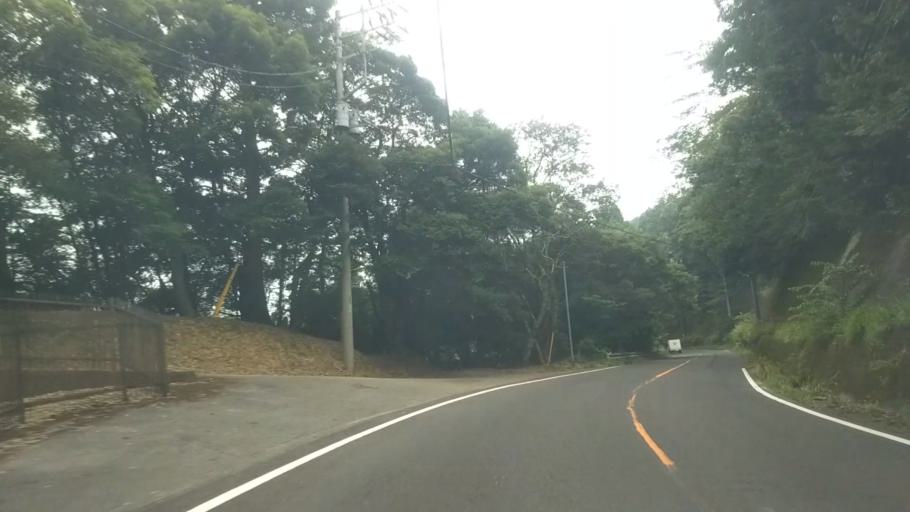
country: JP
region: Chiba
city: Kawaguchi
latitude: 35.2172
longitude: 140.0730
